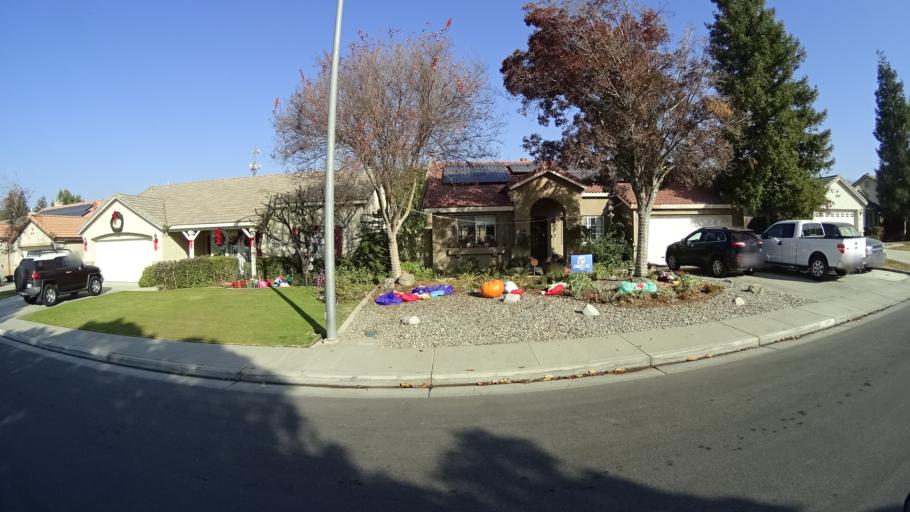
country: US
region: California
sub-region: Kern County
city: Greenacres
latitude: 35.3643
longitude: -119.1111
